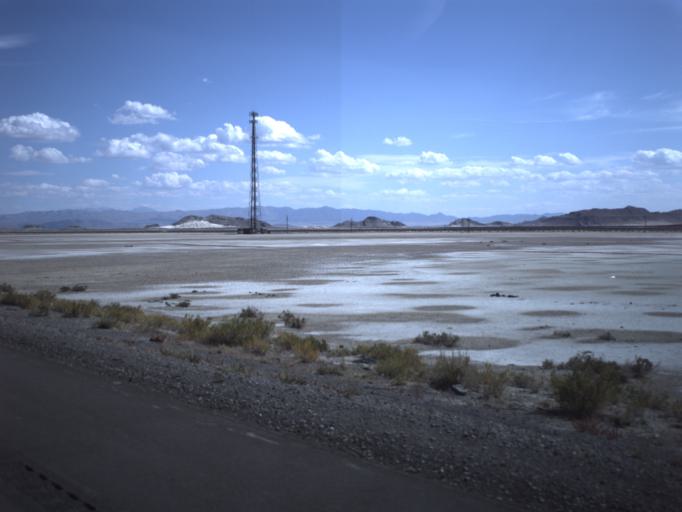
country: US
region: Utah
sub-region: Tooele County
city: Wendover
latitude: 40.7276
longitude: -113.3381
